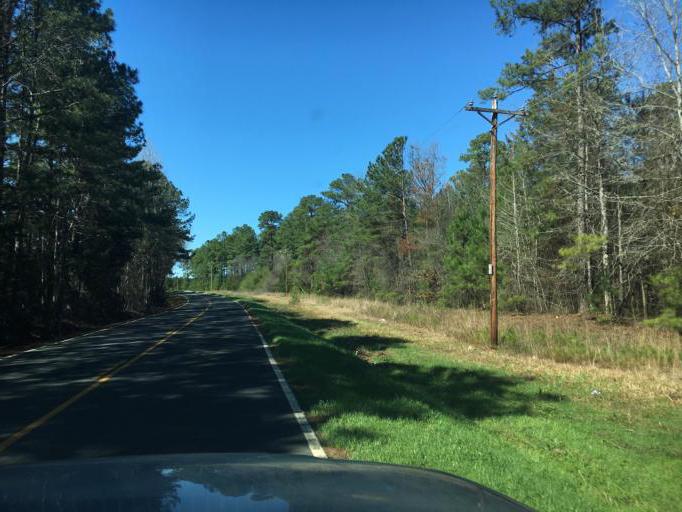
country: US
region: South Carolina
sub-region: Greenwood County
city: Ninety Six
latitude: 34.2883
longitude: -81.9587
